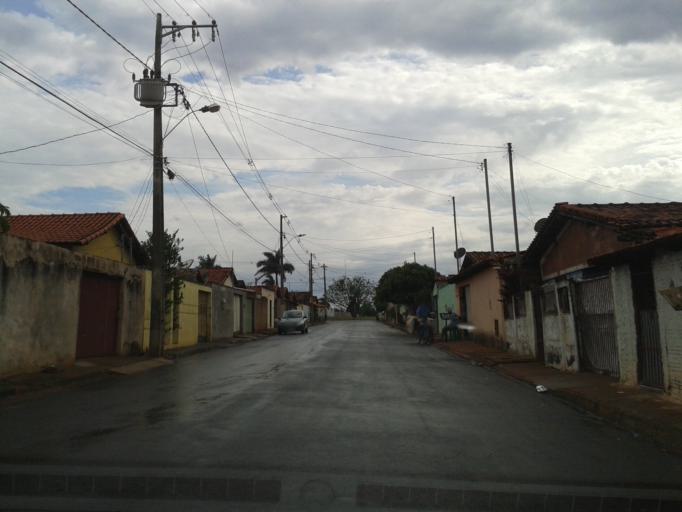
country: BR
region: Minas Gerais
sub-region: Centralina
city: Centralina
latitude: -18.7292
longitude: -49.1961
